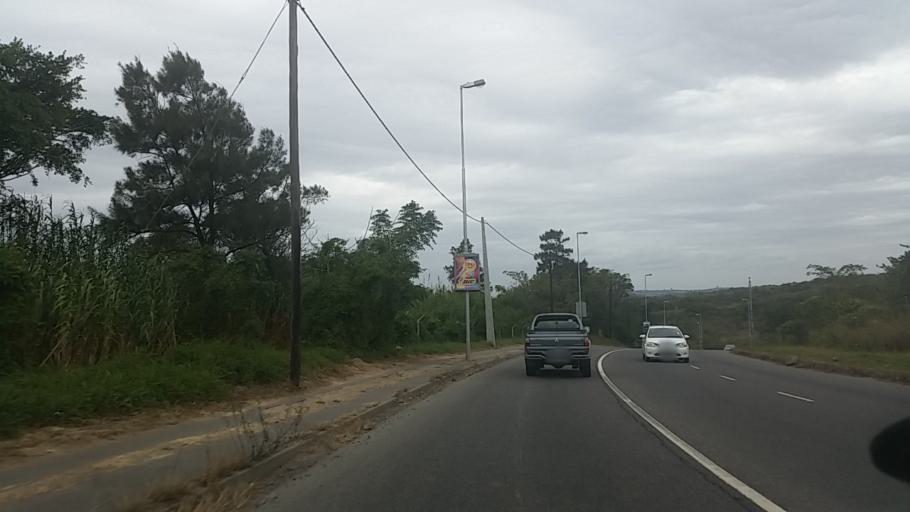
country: ZA
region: KwaZulu-Natal
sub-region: eThekwini Metropolitan Municipality
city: Berea
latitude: -29.8544
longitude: 30.9342
